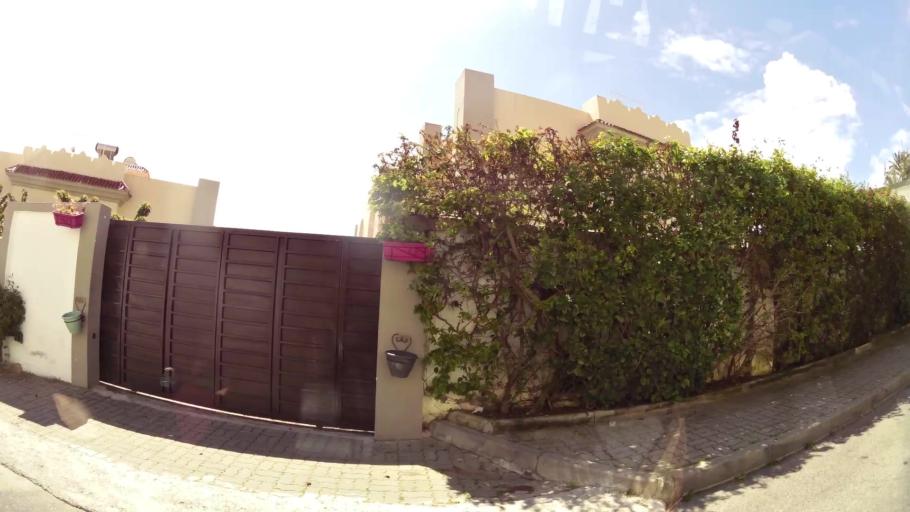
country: MA
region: Tanger-Tetouan
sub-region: Tanger-Assilah
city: Tangier
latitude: 35.7876
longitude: -5.8366
